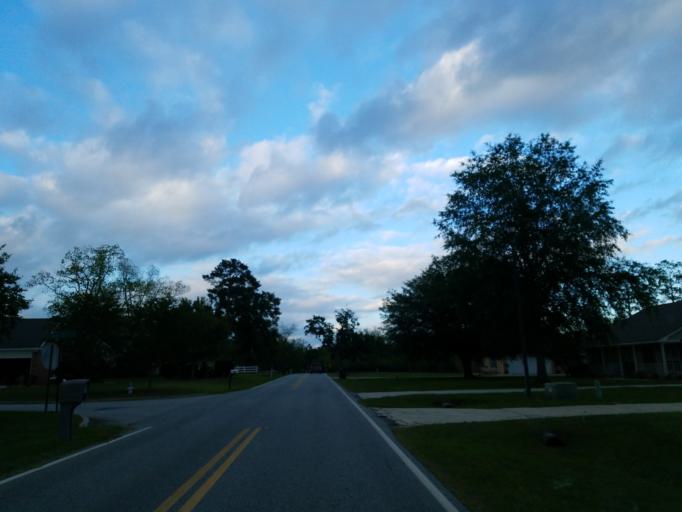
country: US
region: Georgia
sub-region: Lowndes County
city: Remerton
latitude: 30.9052
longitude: -83.3469
